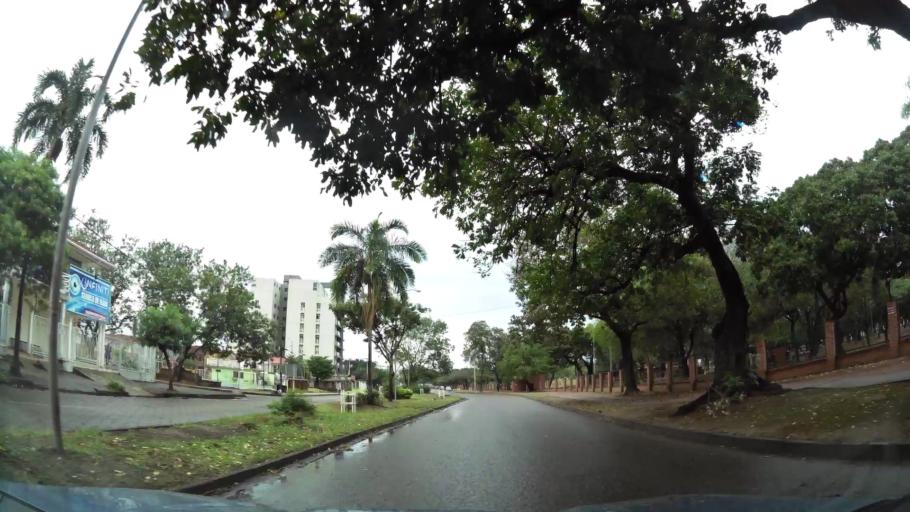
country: BO
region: Santa Cruz
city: Santa Cruz de la Sierra
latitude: -17.7930
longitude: -63.1701
